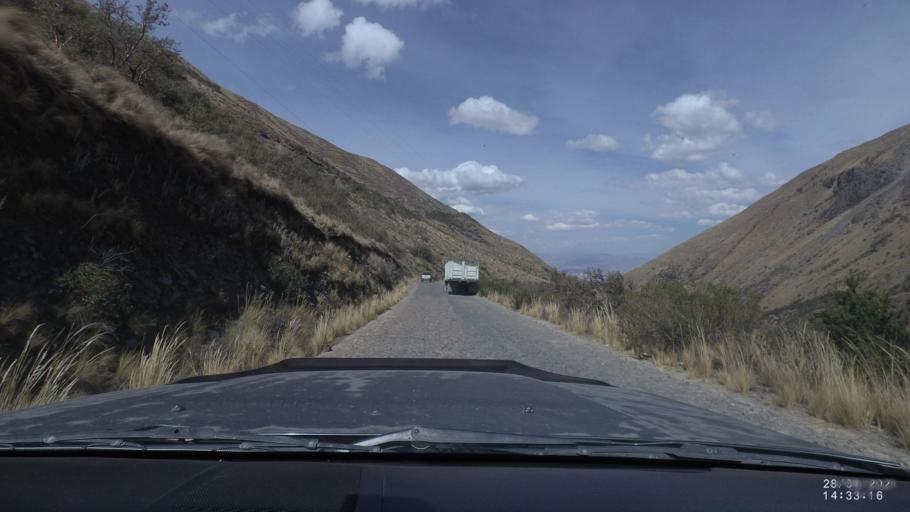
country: BO
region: Cochabamba
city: Sipe Sipe
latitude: -17.2679
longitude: -66.3420
